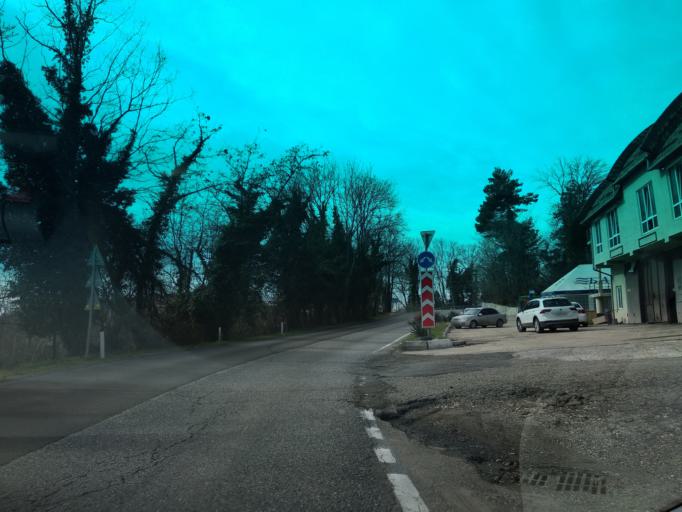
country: RU
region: Krasnodarskiy
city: Shepsi
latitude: 44.0828
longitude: 39.1313
